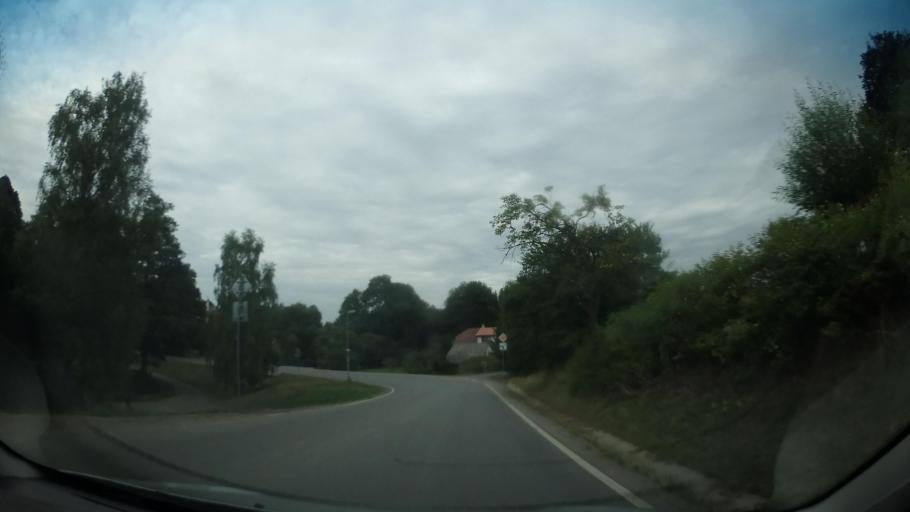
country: CZ
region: Pardubicky
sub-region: Okres Chrudim
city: Sec
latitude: 49.8136
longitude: 15.7206
